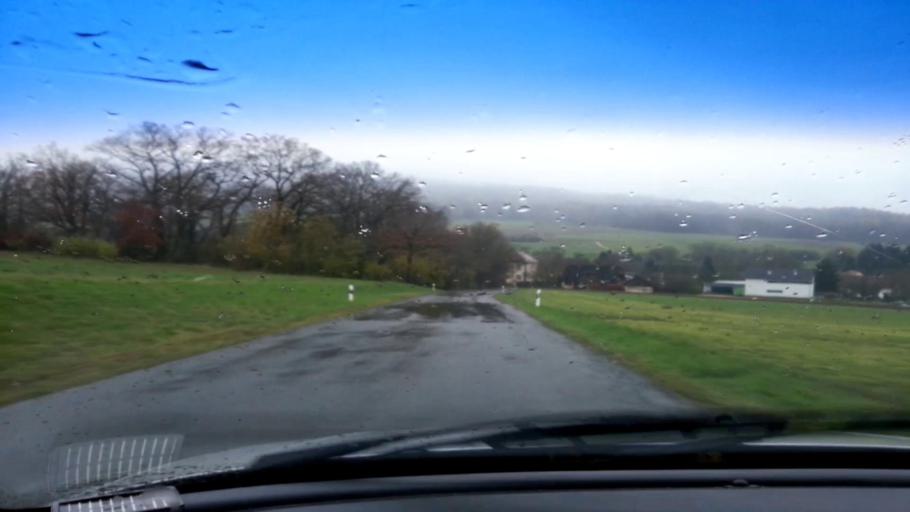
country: DE
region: Bavaria
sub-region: Upper Franconia
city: Schesslitz
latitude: 49.9528
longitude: 11.0364
